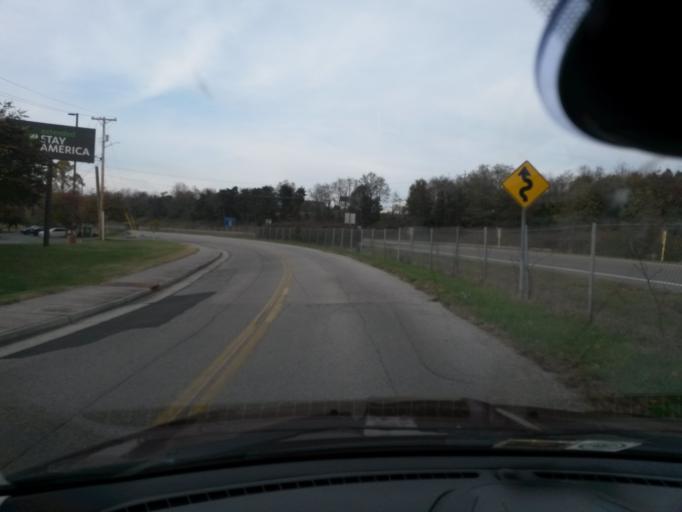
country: US
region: Virginia
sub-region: Roanoke County
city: Hollins
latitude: 37.3101
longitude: -79.9764
